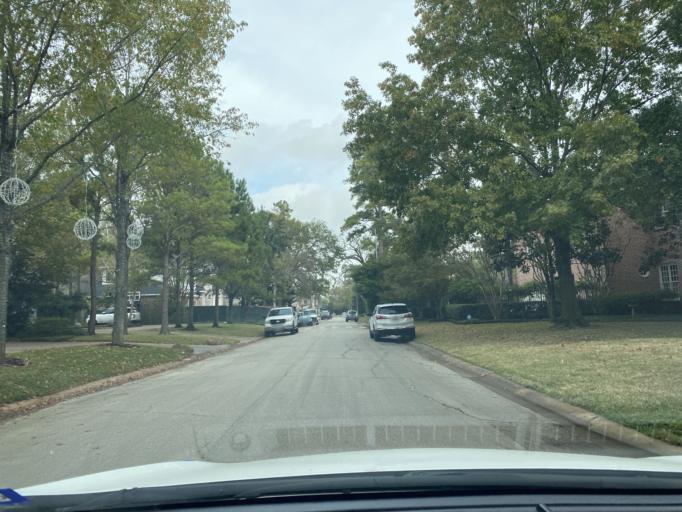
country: US
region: Texas
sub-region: Harris County
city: Hunters Creek Village
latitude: 29.7663
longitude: -95.4710
